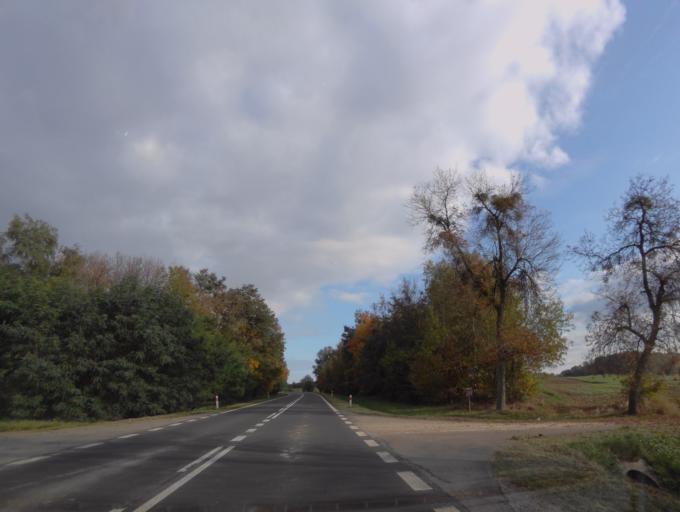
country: PL
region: Lublin Voivodeship
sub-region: Powiat bilgorajski
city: Turobin
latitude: 50.7945
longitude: 22.6836
